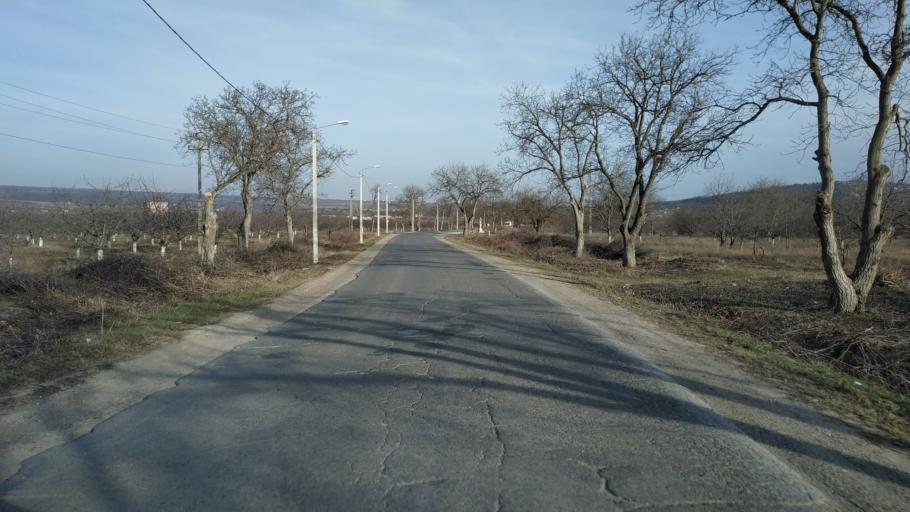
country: MD
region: Chisinau
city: Vatra
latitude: 47.0688
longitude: 28.7222
